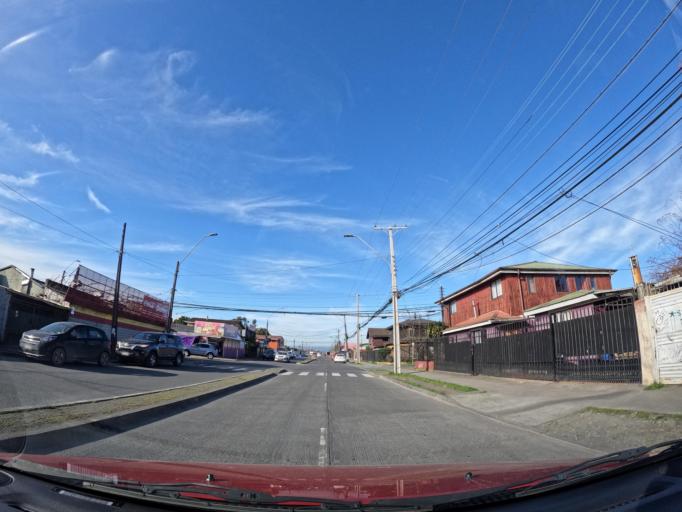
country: CL
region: Biobio
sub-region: Provincia de Concepcion
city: Talcahuano
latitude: -36.7472
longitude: -73.0936
